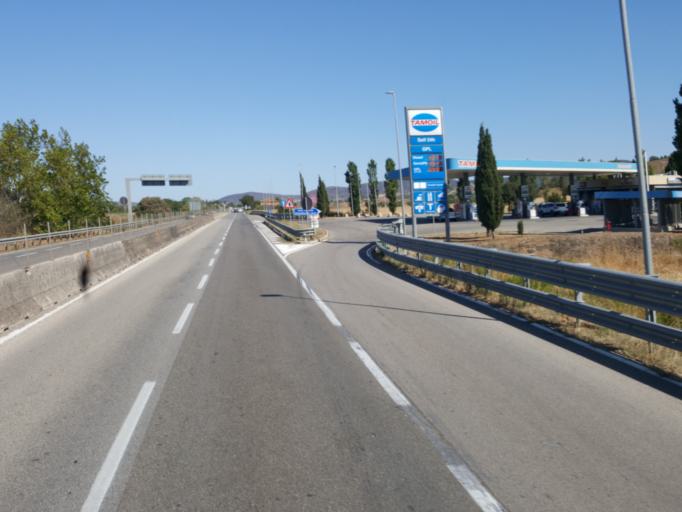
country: IT
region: Tuscany
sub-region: Provincia di Grosseto
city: Fonteblanda
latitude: 42.5730
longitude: 11.1673
